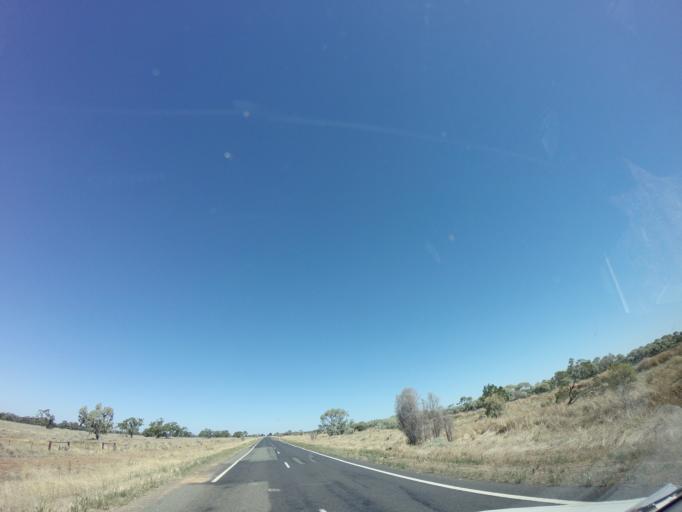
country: AU
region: New South Wales
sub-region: Bogan
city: Nyngan
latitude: -31.6248
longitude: 147.3146
